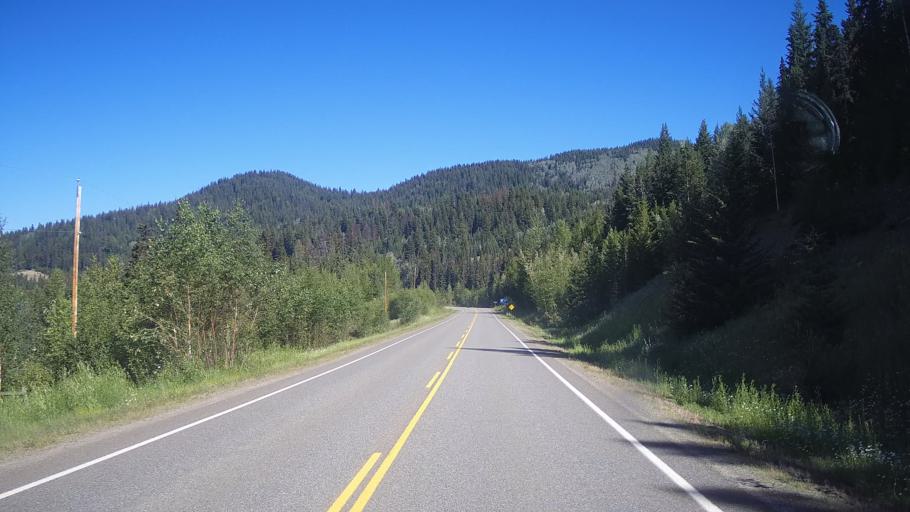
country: CA
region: British Columbia
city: Kamloops
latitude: 51.4665
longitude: -120.5318
